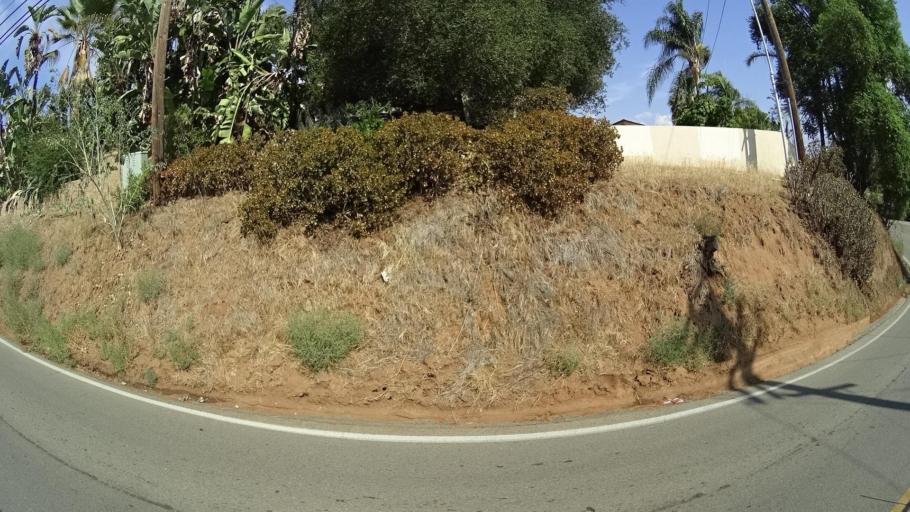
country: US
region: California
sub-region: San Diego County
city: Escondido
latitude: 33.0983
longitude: -117.0665
